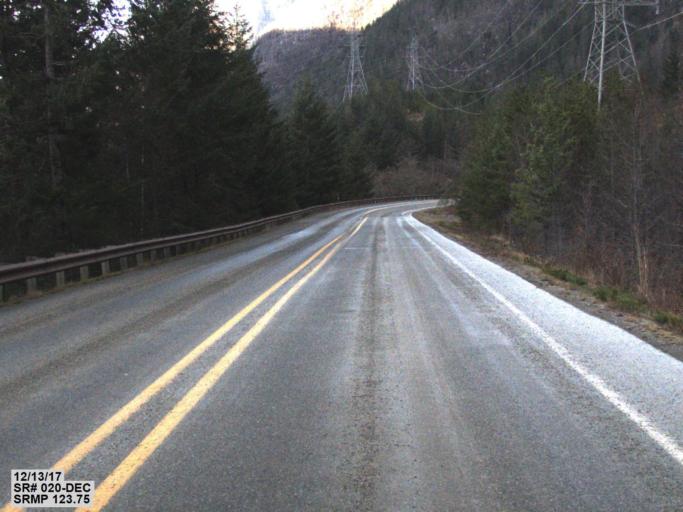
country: US
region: Washington
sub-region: Snohomish County
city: Darrington
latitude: 48.7006
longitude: -121.2040
